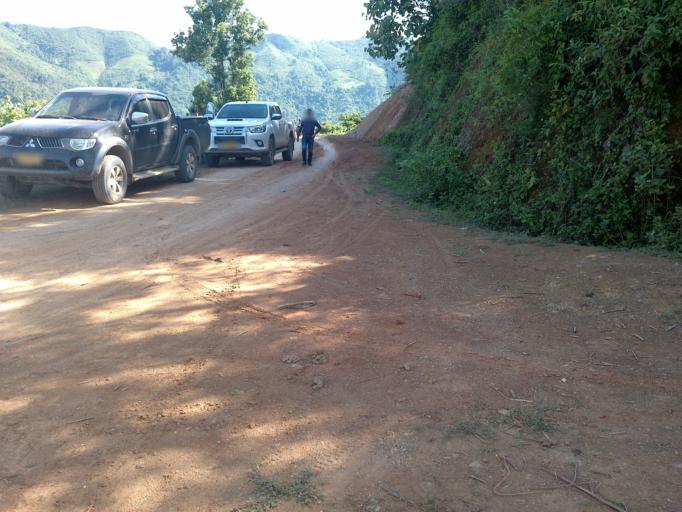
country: TH
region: Nan
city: Chaloem Phra Kiat
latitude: 19.9449
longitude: 101.1615
